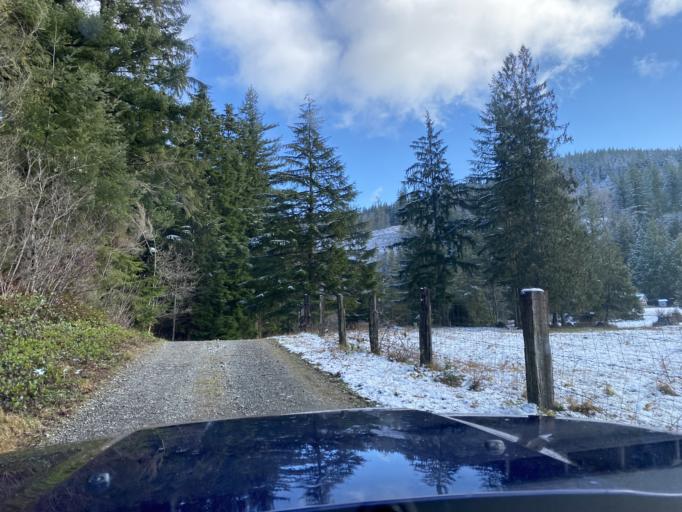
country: US
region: Washington
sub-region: King County
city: Snoqualmie
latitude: 47.5051
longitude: -121.8753
